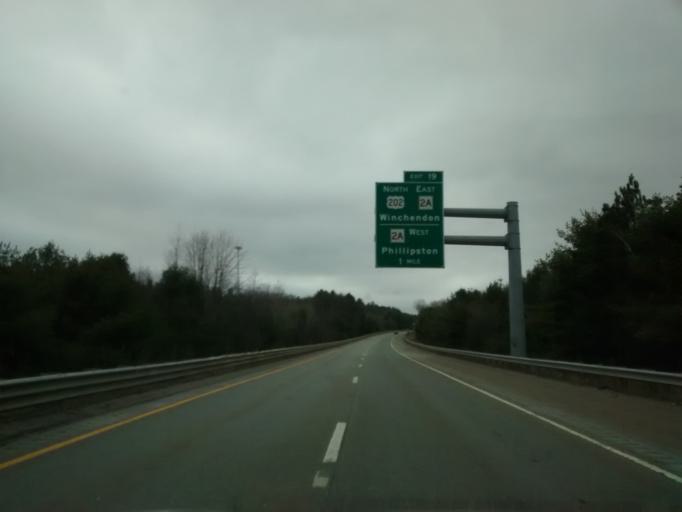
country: US
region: Massachusetts
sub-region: Worcester County
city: Phillipston
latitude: 42.5681
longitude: -72.1031
